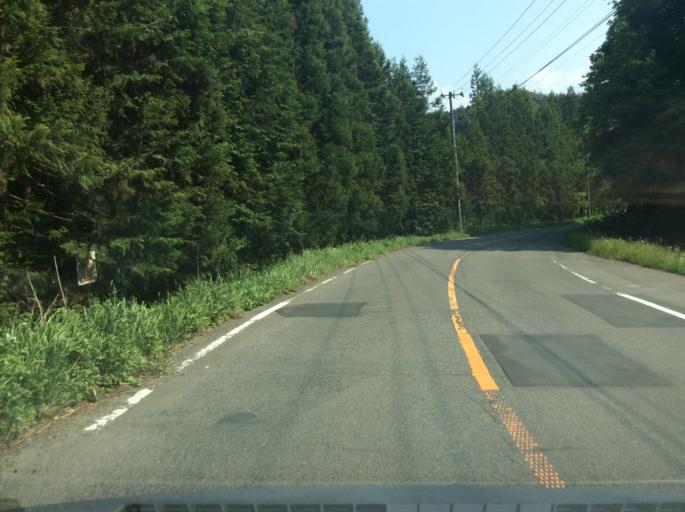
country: JP
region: Tochigi
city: Kuroiso
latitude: 37.0833
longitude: 140.2245
